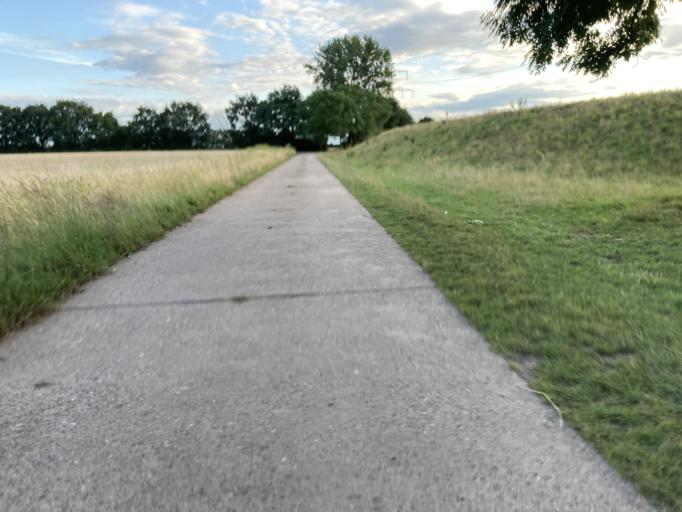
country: DE
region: Lower Saxony
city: Verden
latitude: 52.9163
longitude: 9.1950
